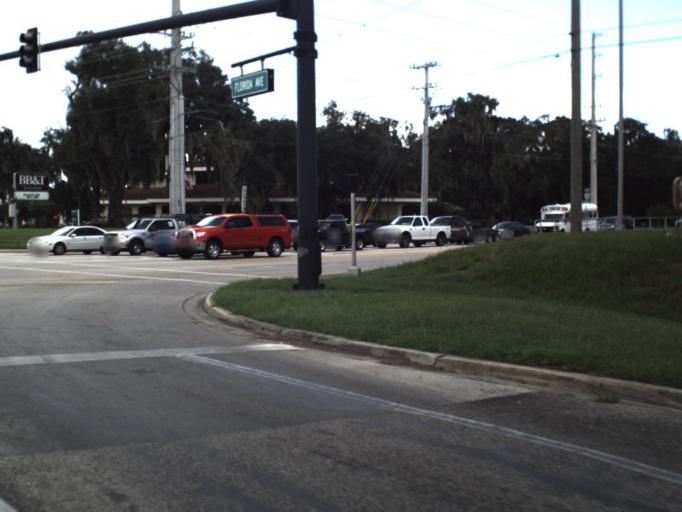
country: US
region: Florida
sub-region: Polk County
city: Medulla
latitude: 27.9531
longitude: -81.9691
